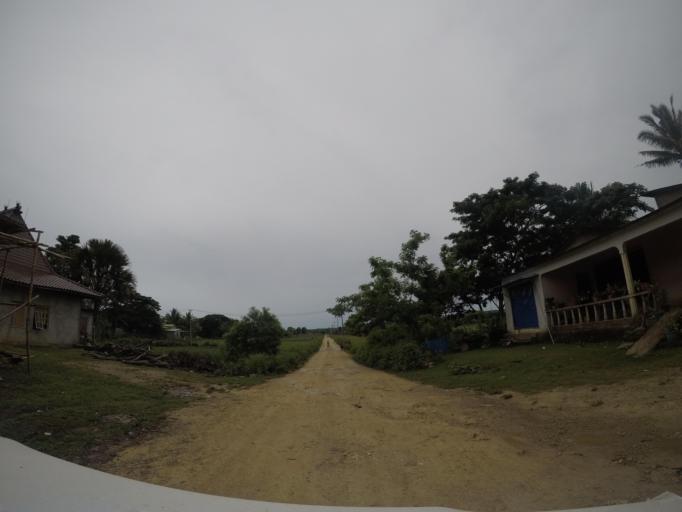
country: TL
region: Lautem
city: Lospalos
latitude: -8.5218
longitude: 127.0026
